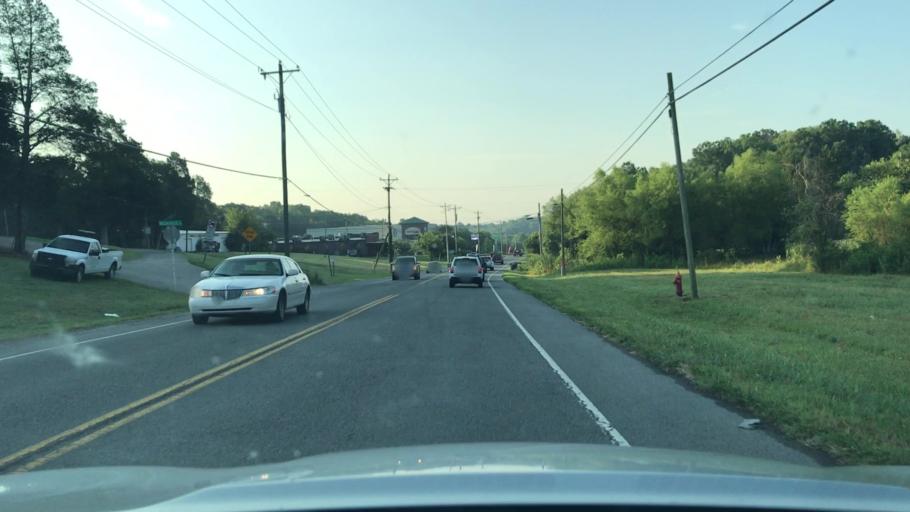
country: US
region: Tennessee
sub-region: Williamson County
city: Brentwood Estates
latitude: 36.0174
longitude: -86.7073
